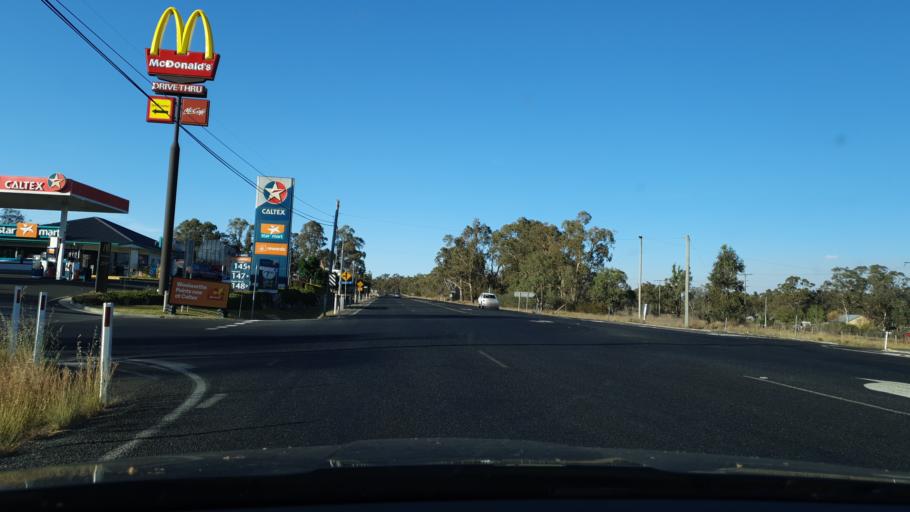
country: AU
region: Queensland
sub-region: Southern Downs
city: Stanthorpe
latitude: -28.6318
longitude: 151.9539
